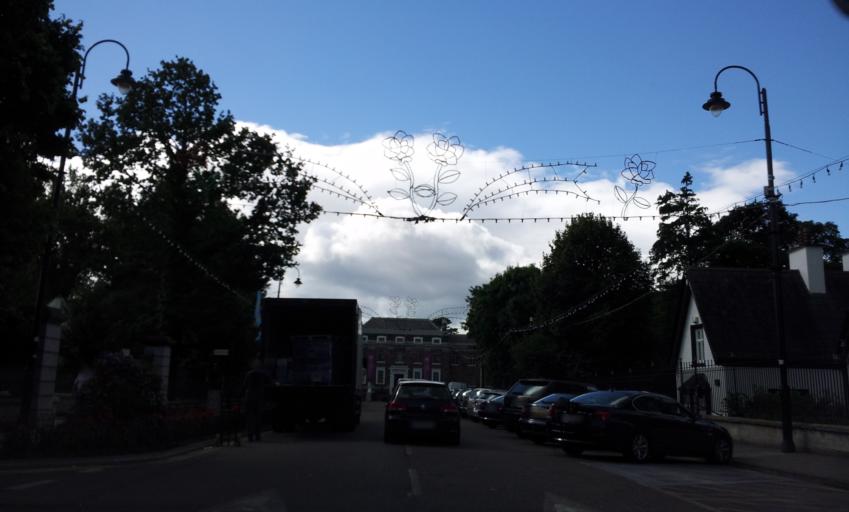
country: IE
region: Munster
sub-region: Ciarrai
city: Tralee
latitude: 52.2680
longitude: -9.7056
